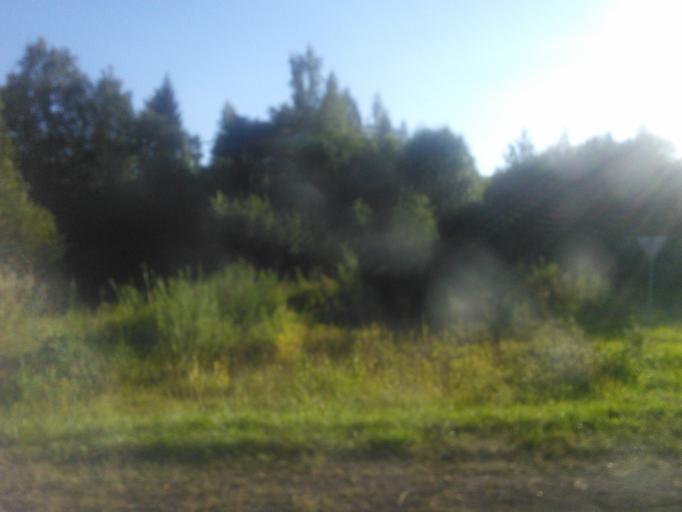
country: RU
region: Jaroslavl
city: Poshekhon'ye
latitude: 58.3761
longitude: 38.9997
